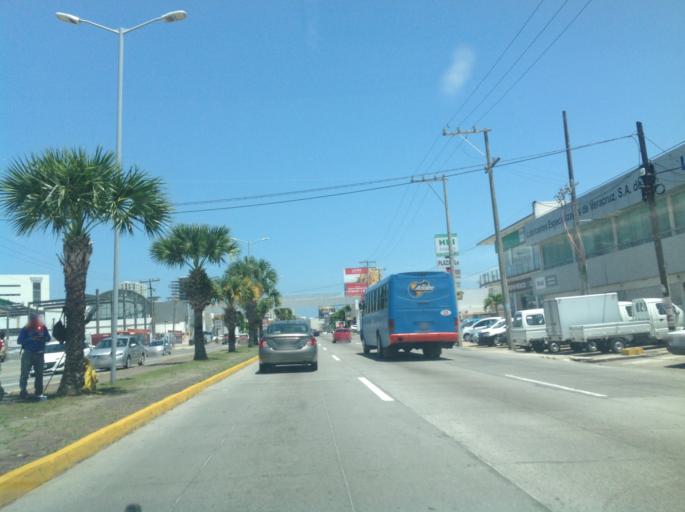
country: MX
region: Veracruz
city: Boca del Rio
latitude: 19.1406
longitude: -96.1136
